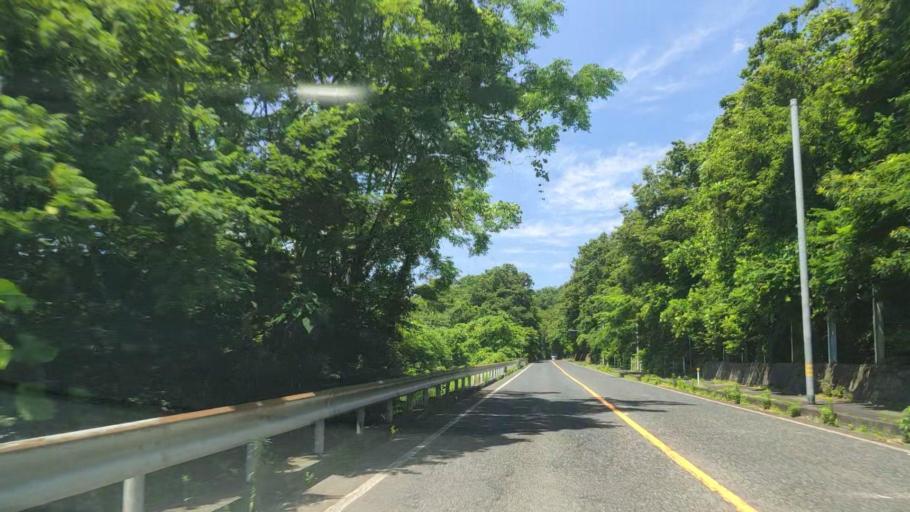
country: JP
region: Tottori
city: Tottori
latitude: 35.5254
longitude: 134.2304
